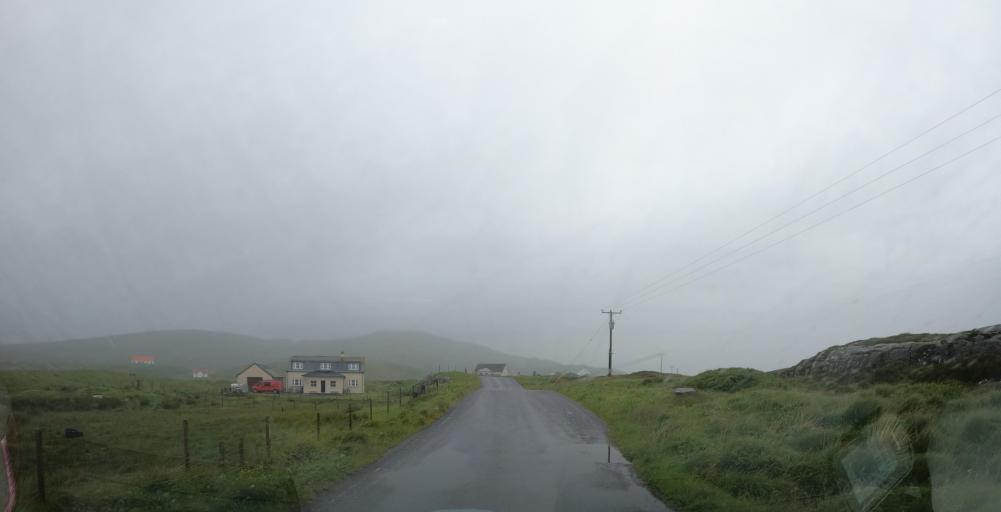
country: GB
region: Scotland
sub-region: Eilean Siar
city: Barra
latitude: 57.0095
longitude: -7.4220
